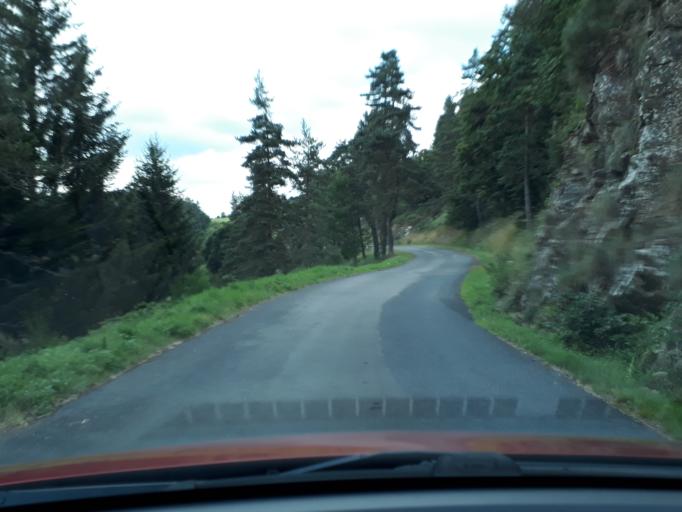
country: FR
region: Auvergne
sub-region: Departement de la Haute-Loire
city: Le Monastier-sur-Gazeille
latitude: 44.8265
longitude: 3.9448
